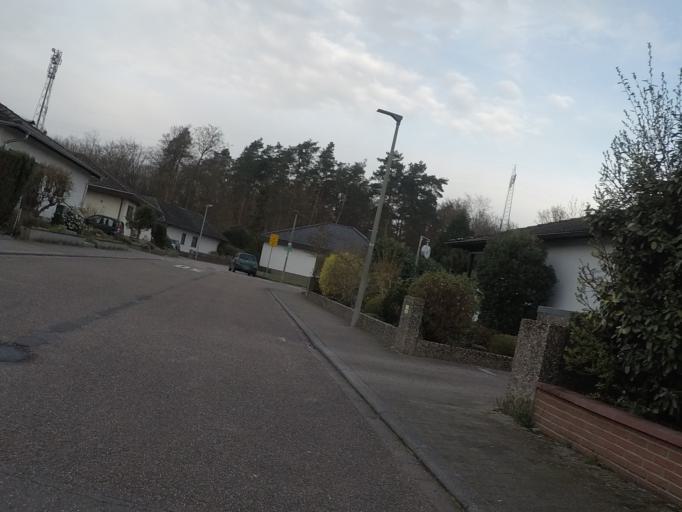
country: DE
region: Rheinland-Pfalz
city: Worth am Rhein
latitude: 49.0537
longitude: 8.2396
